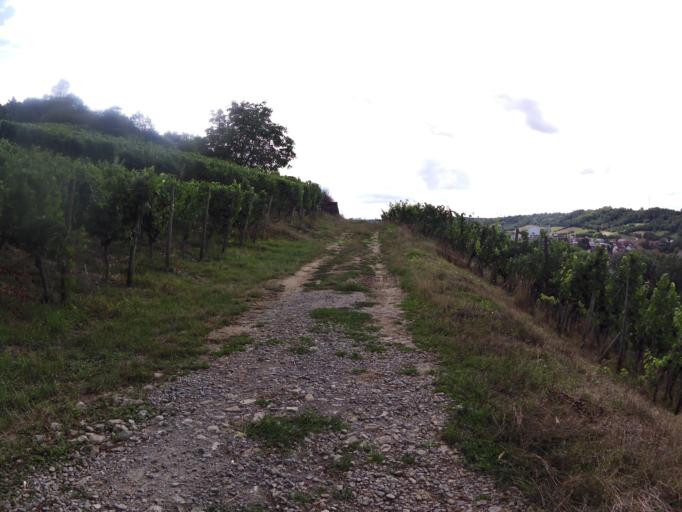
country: DE
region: Bavaria
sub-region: Regierungsbezirk Unterfranken
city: Sommerhausen
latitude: 49.6849
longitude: 10.0322
